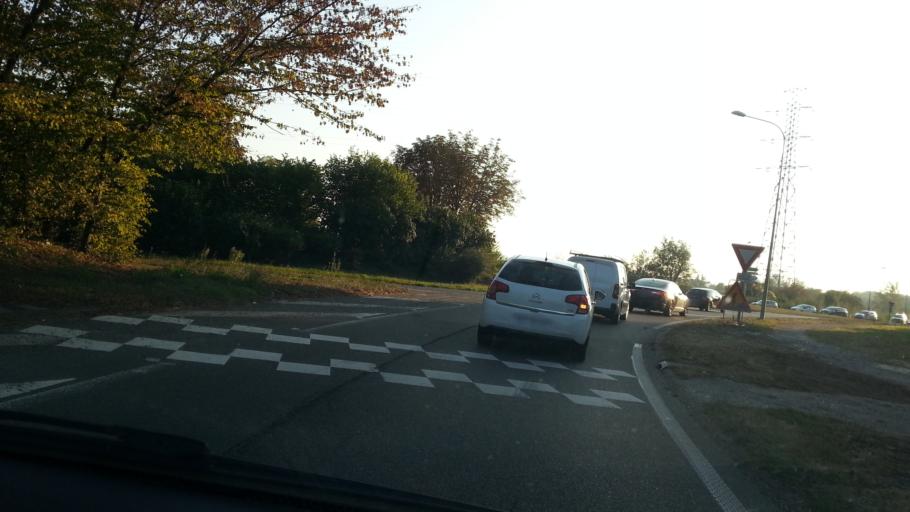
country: FR
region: Picardie
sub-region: Departement de l'Oise
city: Les Ageux
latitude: 49.3249
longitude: 2.6033
